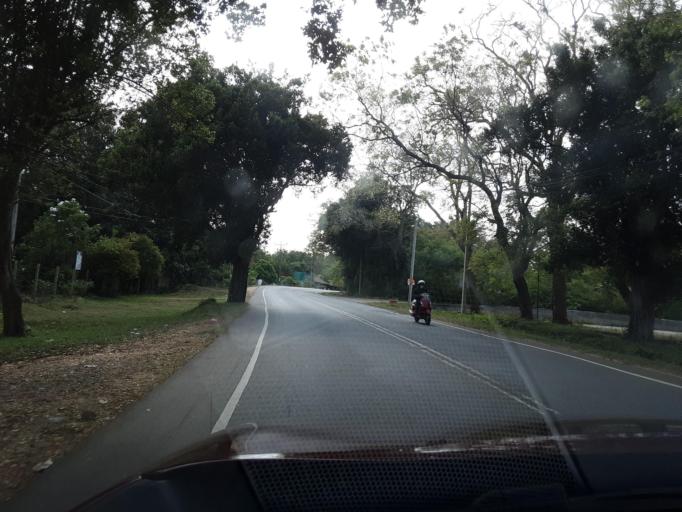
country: LK
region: Uva
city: Haputale
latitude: 6.3459
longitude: 81.1996
